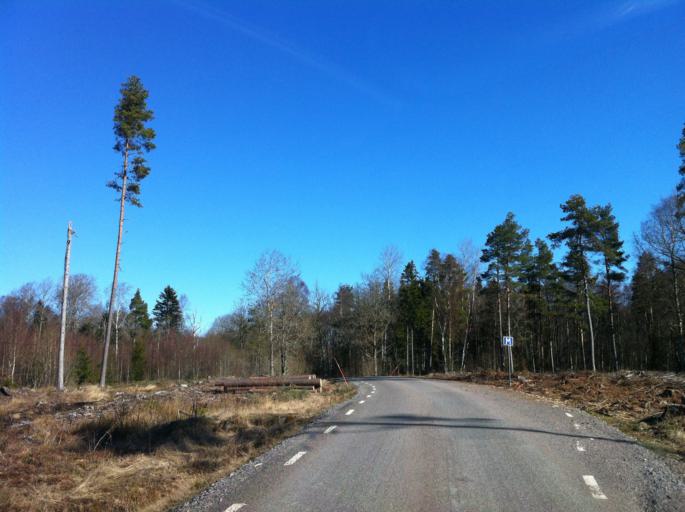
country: SE
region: Vaestra Goetaland
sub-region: Grastorps Kommun
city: Graestorp
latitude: 58.4458
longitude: 12.6158
